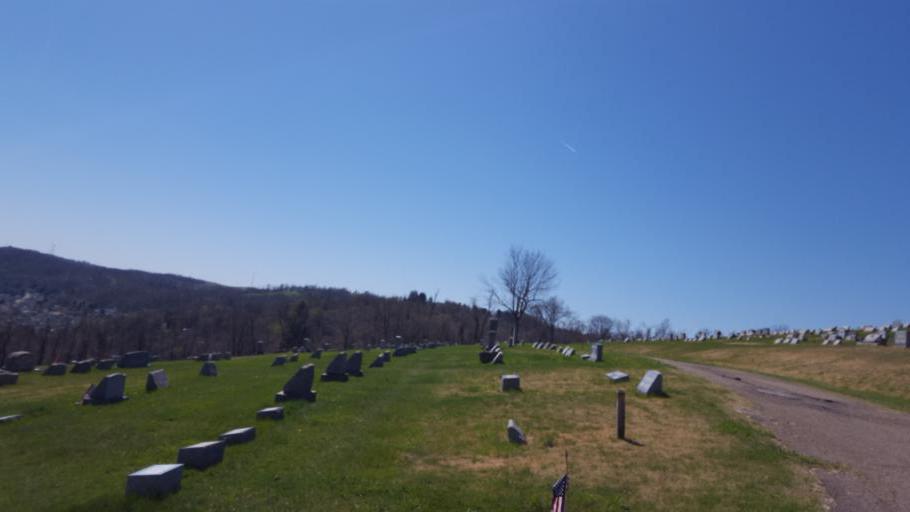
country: US
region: Ohio
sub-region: Belmont County
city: Martins Ferry
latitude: 40.1057
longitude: -80.7238
